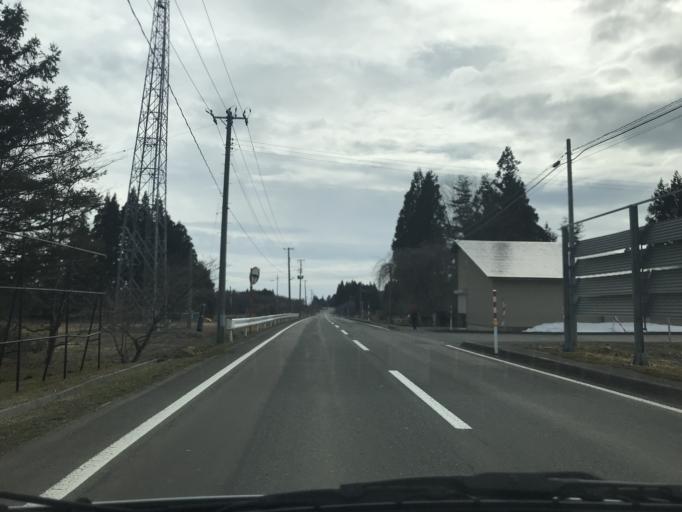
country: JP
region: Iwate
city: Hanamaki
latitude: 39.3818
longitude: 141.0080
